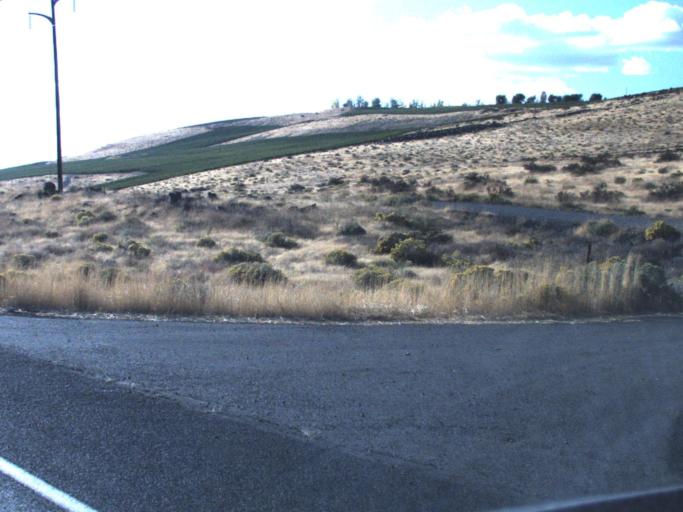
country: US
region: Oregon
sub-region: Morrow County
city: Boardman
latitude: 45.8806
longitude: -119.7316
